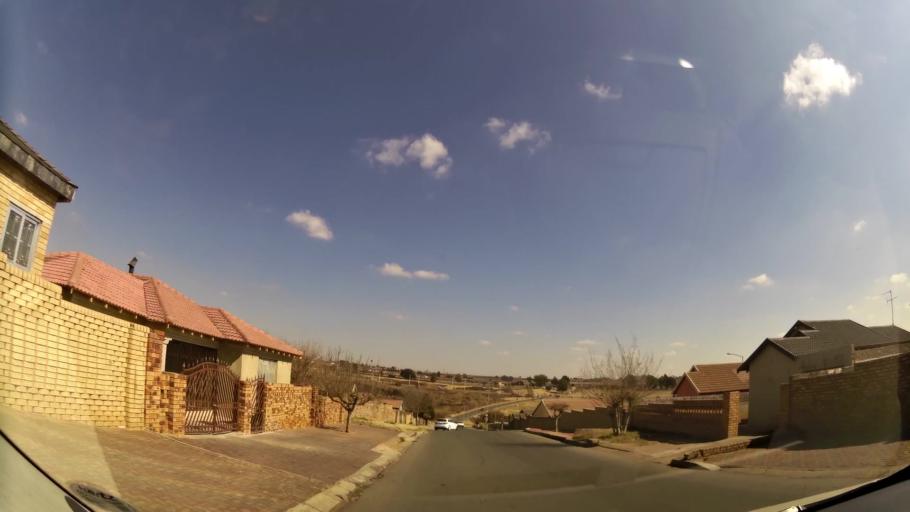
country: ZA
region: Gauteng
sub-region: West Rand District Municipality
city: Krugersdorp
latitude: -26.1556
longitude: 27.7665
